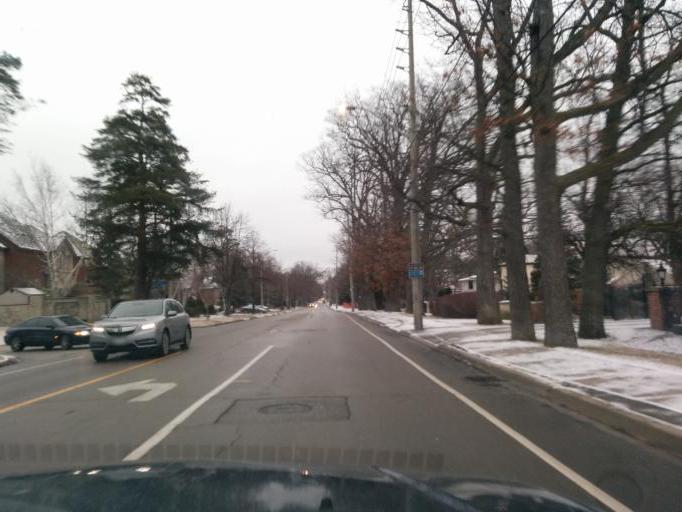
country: CA
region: Ontario
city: Mississauga
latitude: 43.5360
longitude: -79.6469
